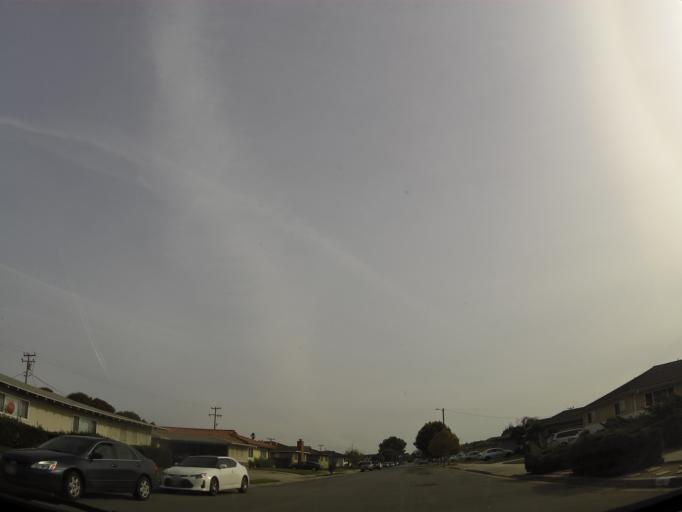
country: US
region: California
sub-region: Monterey County
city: Salinas
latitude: 36.6666
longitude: -121.6759
